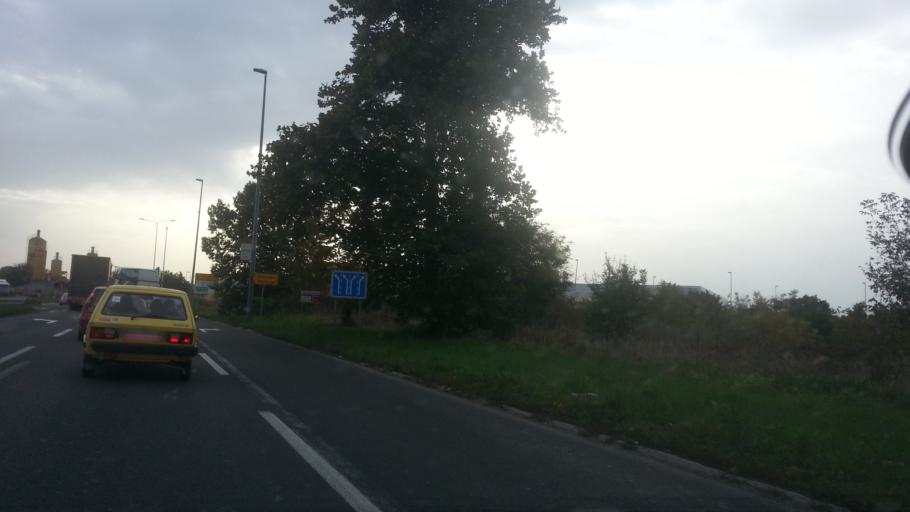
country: RS
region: Central Serbia
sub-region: Belgrade
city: Zemun
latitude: 44.8514
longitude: 20.3726
